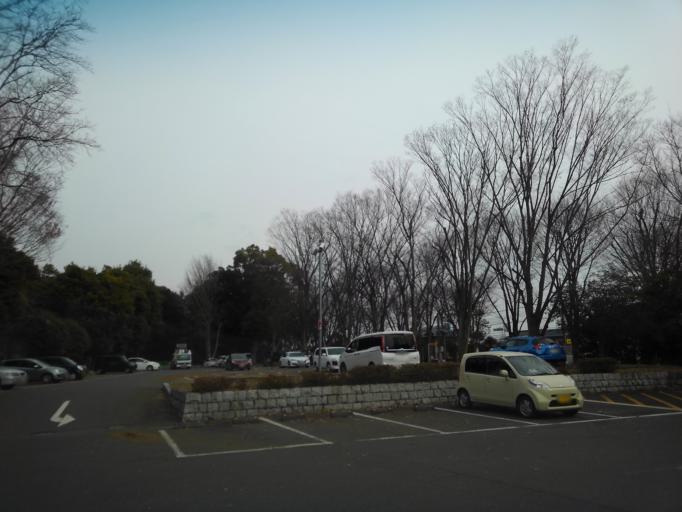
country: JP
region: Saitama
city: Tokorozawa
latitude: 35.7960
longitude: 139.4748
